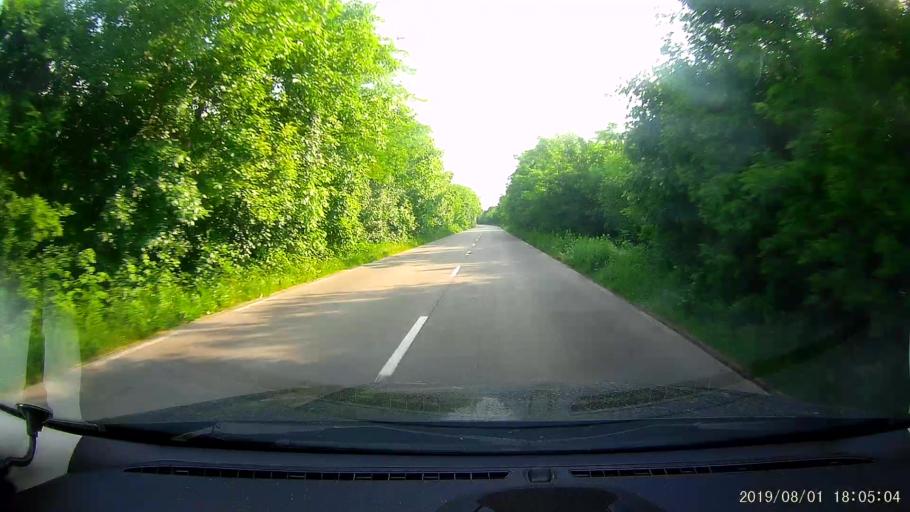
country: BG
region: Silistra
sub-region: Obshtina Alfatar
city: Alfatar
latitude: 43.8973
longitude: 27.2677
